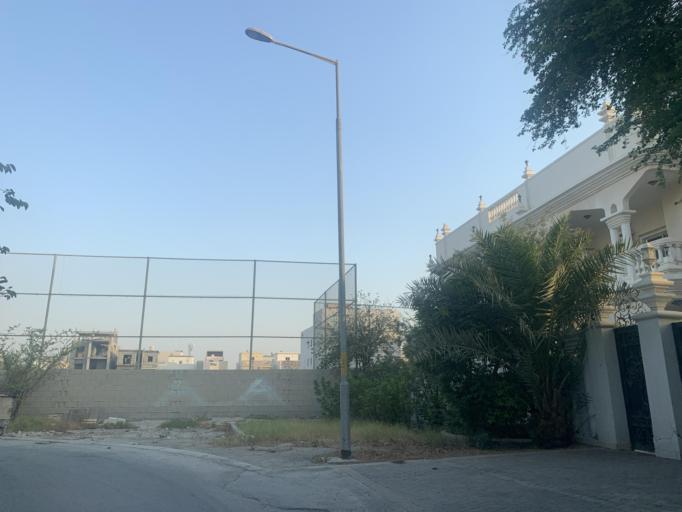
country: BH
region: Manama
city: Jidd Hafs
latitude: 26.2137
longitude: 50.5290
